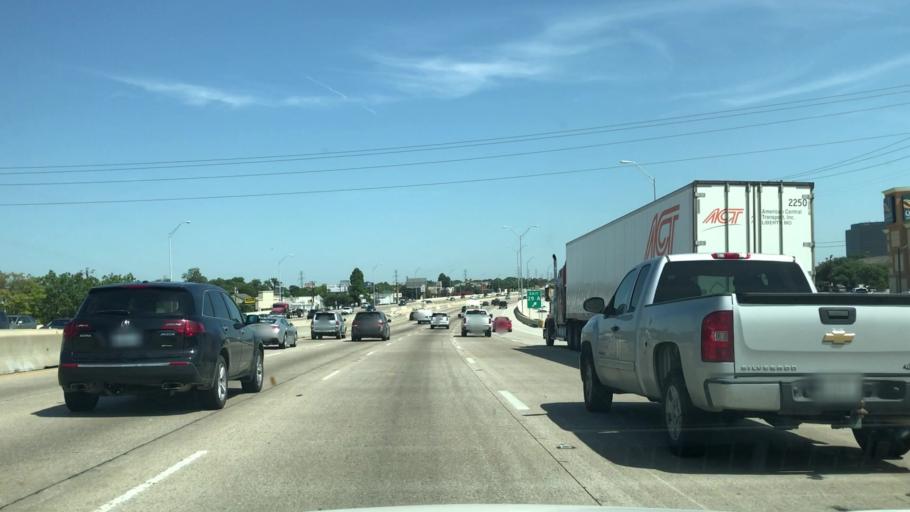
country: US
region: Texas
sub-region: Collin County
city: Plano
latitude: 33.0211
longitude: -96.7096
